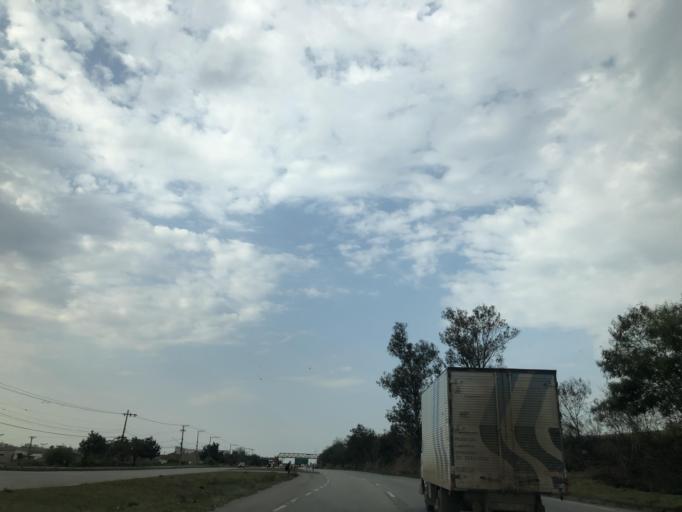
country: BR
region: Sao Paulo
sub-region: Votorantim
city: Votorantim
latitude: -23.5619
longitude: -47.4912
